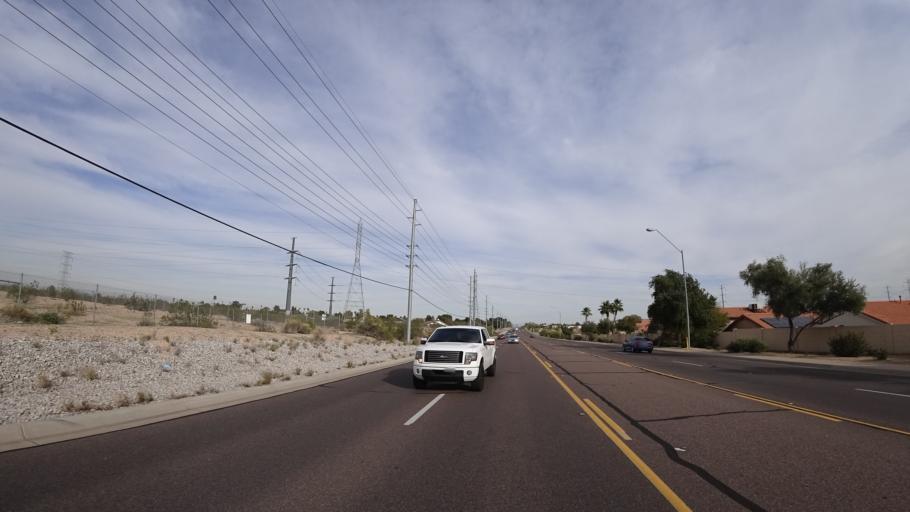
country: US
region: Arizona
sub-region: Maricopa County
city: Youngtown
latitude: 33.5654
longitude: -112.3030
